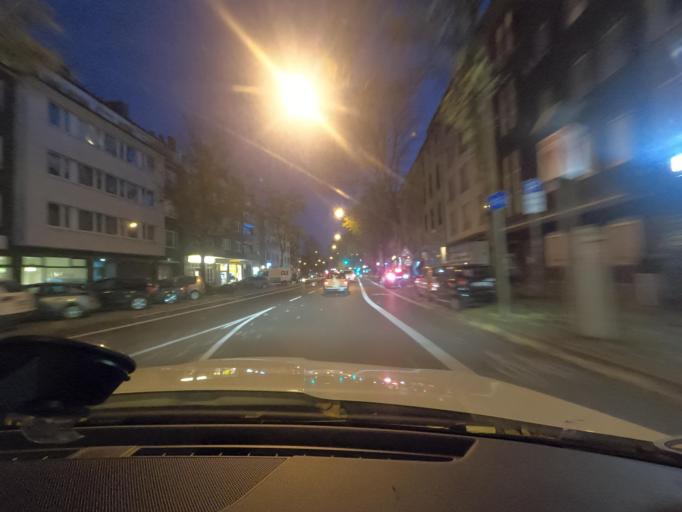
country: DE
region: North Rhine-Westphalia
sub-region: Regierungsbezirk Dusseldorf
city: Dusseldorf
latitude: 51.2451
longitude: 6.7859
